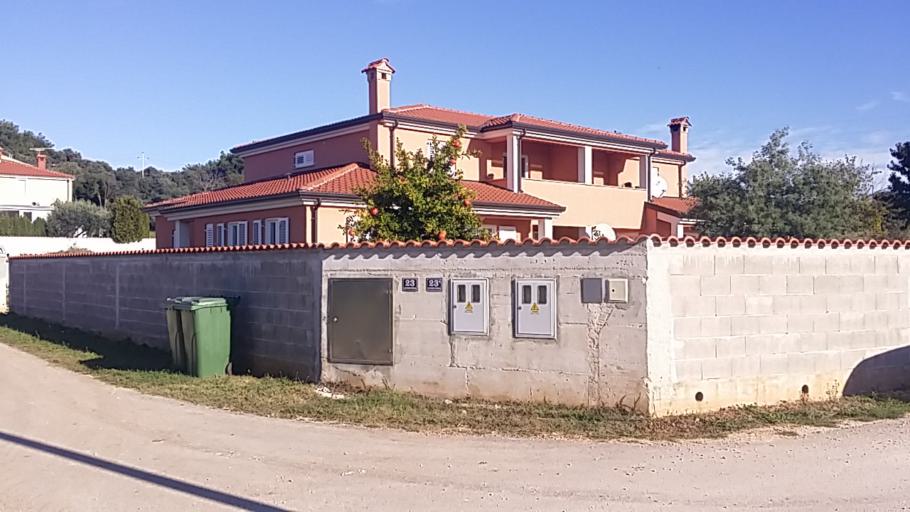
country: HR
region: Istarska
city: Vrsar
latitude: 45.1402
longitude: 13.6180
